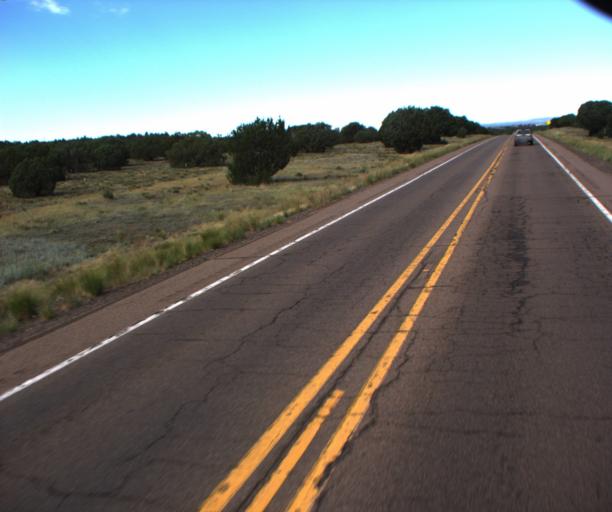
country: US
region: Arizona
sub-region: Navajo County
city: Show Low
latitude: 34.2629
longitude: -109.9754
